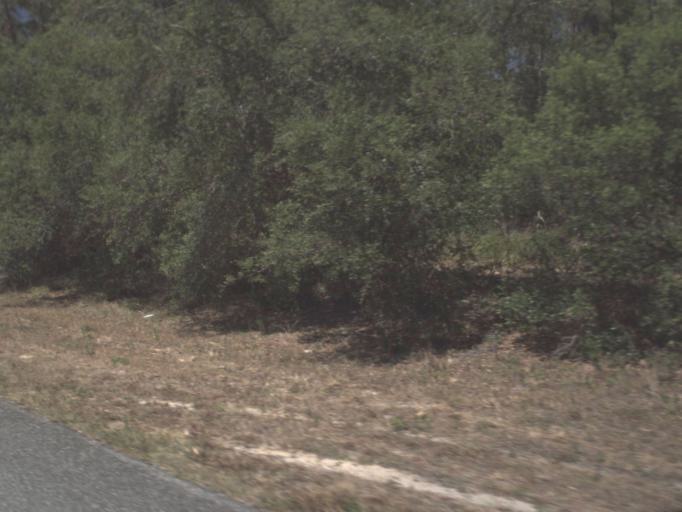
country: US
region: Florida
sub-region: Lake County
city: Astor
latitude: 29.1638
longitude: -81.6403
